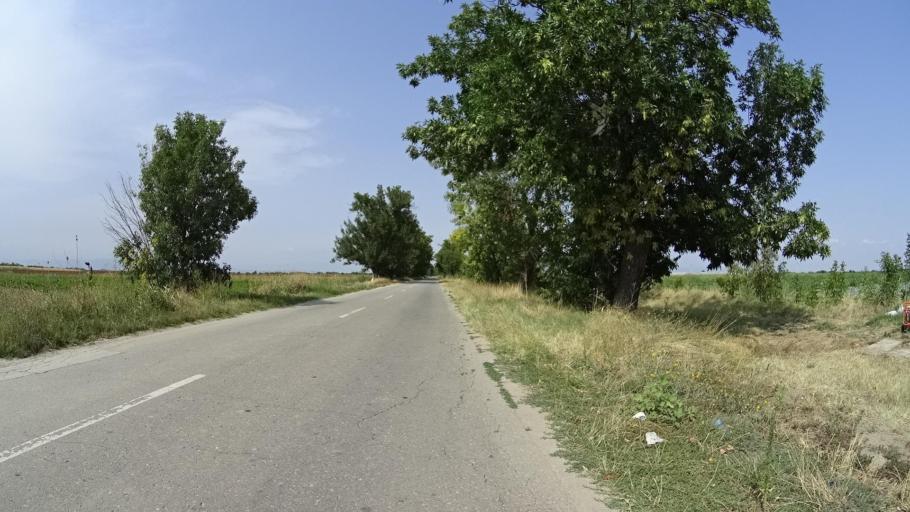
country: BG
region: Plovdiv
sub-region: Obshtina Plovdiv
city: Plovdiv
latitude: 42.2504
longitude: 24.7973
